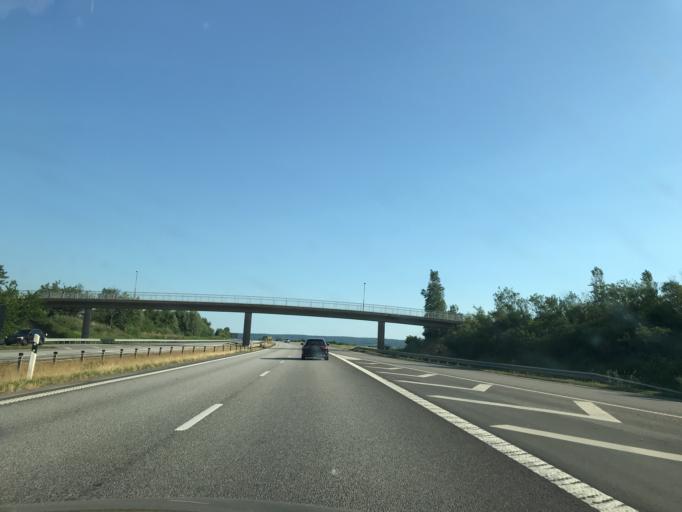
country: SE
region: Skane
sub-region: Angelholms Kommun
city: AEngelholm
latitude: 56.2537
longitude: 12.8983
